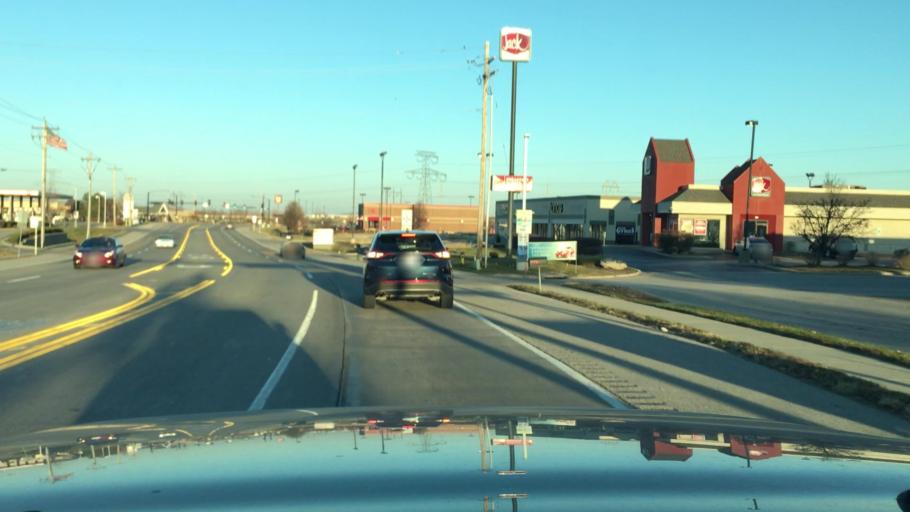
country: US
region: Missouri
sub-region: Saint Charles County
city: Saint Charles
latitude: 38.8197
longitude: -90.5135
